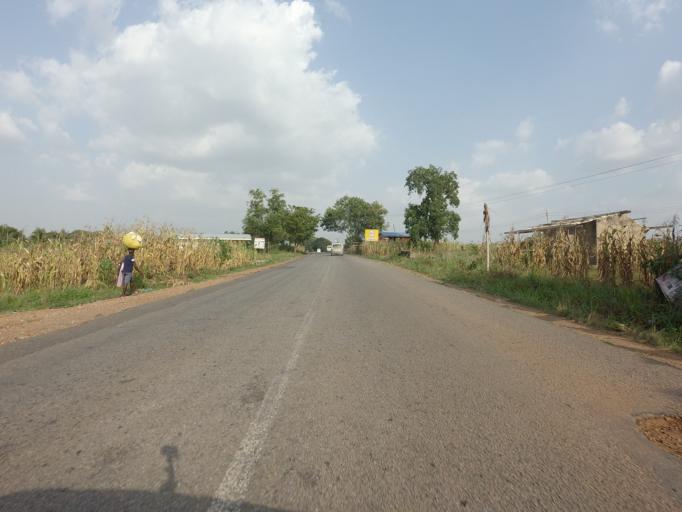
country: GH
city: Akropong
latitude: 6.2431
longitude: 0.1222
